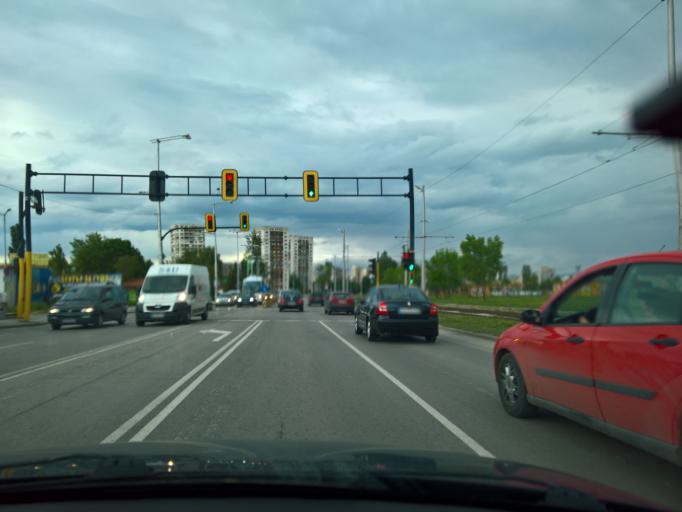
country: BG
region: Sofia-Capital
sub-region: Stolichna Obshtina
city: Sofia
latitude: 42.6891
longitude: 23.2768
